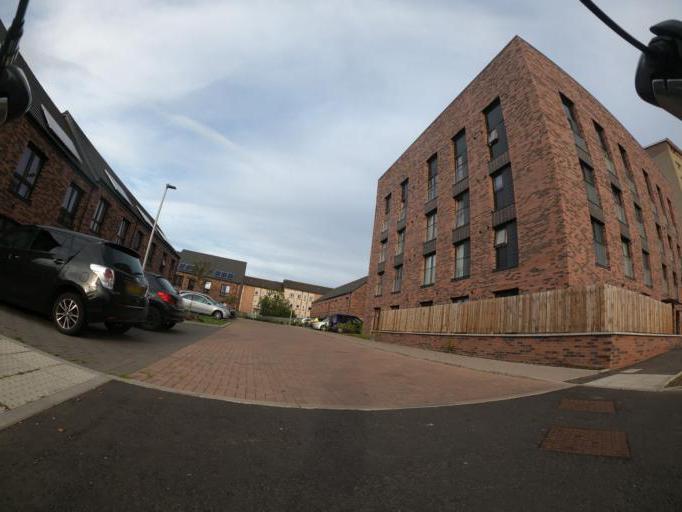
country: GB
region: Scotland
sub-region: Edinburgh
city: Edinburgh
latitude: 55.9715
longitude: -3.2445
